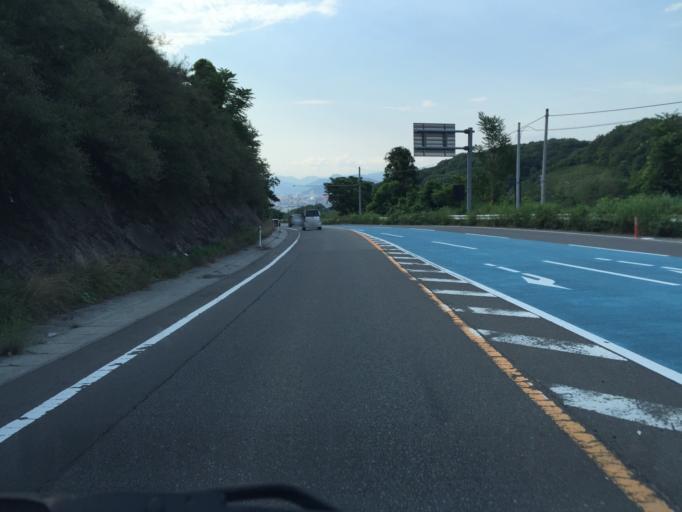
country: JP
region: Fukushima
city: Fukushima-shi
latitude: 37.7118
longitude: 140.4662
